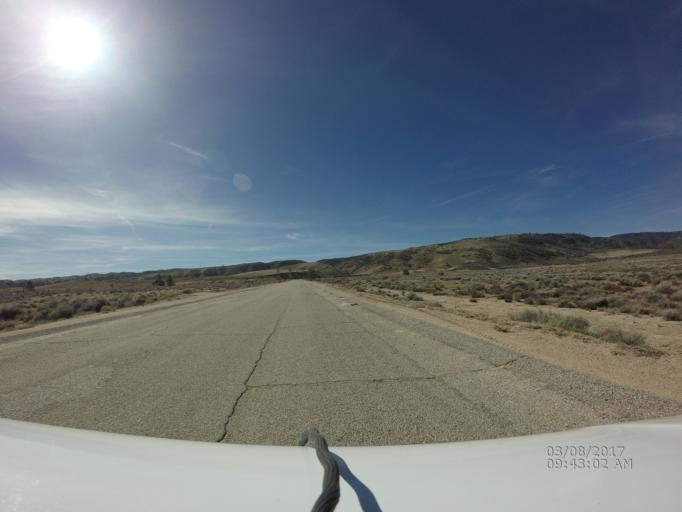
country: US
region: California
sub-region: Los Angeles County
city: Green Valley
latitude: 34.7351
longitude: -118.4752
